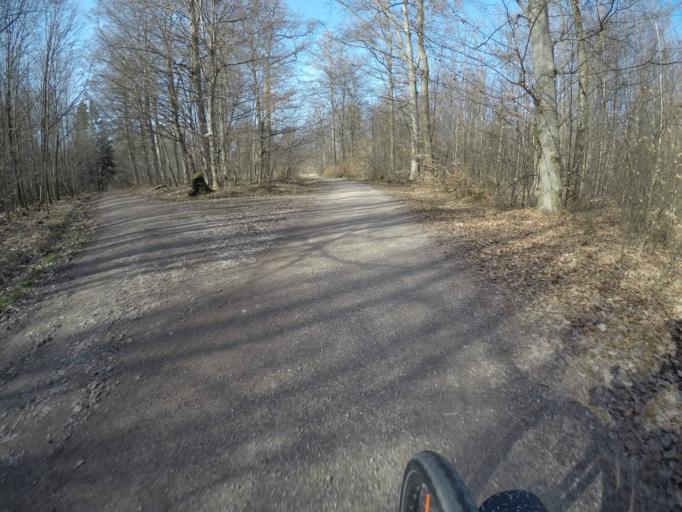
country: DE
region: Baden-Wuerttemberg
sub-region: Regierungsbezirk Stuttgart
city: Hochdorf
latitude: 48.6810
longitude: 9.4664
